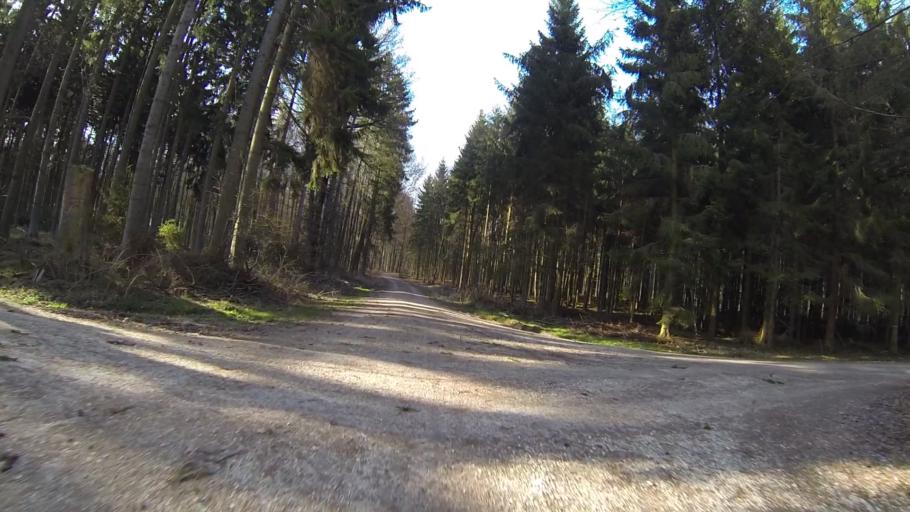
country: DE
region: Baden-Wuerttemberg
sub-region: Regierungsbezirk Stuttgart
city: Niederstotzingen
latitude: 48.5665
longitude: 10.2264
